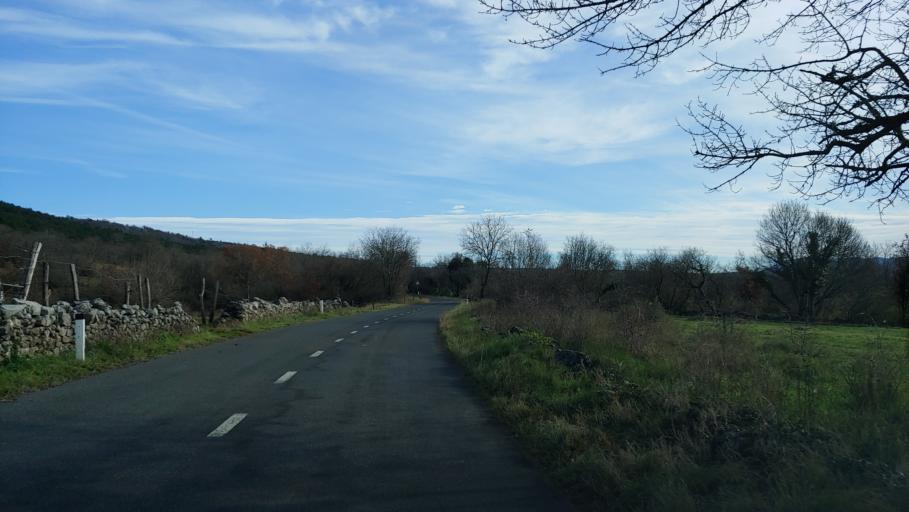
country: IT
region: Friuli Venezia Giulia
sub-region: Provincia di Trieste
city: Sistiana-Visogliano
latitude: 45.8124
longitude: 13.6739
